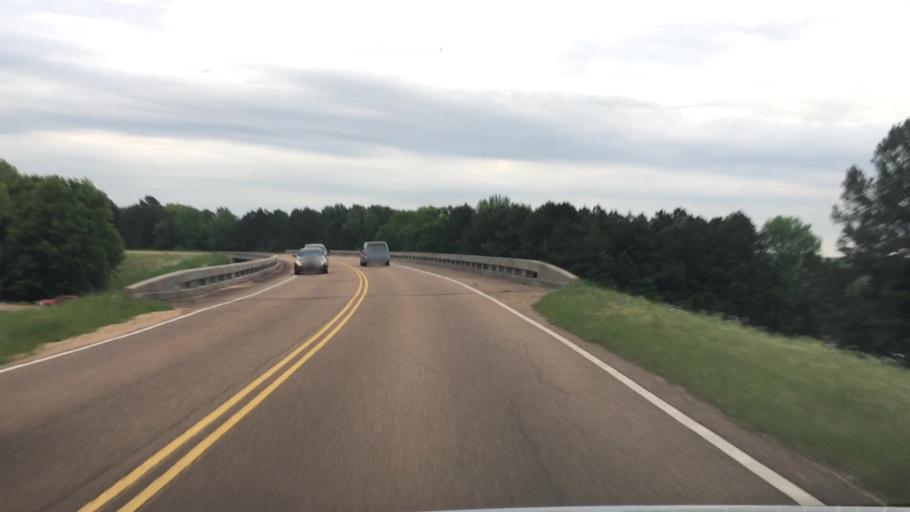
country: US
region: Mississippi
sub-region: Hinds County
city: Clinton
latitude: 32.3810
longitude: -90.2606
